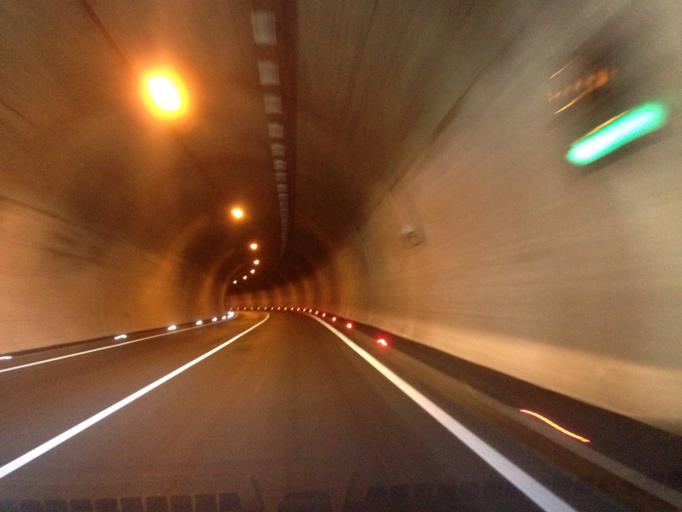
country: AT
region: Tyrol
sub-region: Politischer Bezirk Imst
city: Nassereith
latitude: 47.3098
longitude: 10.8355
